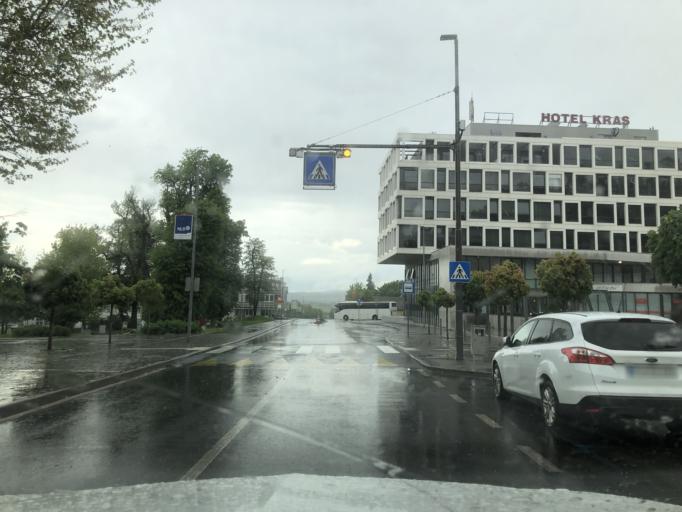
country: SI
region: Postojna
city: Postojna
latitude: 45.7752
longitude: 14.2135
